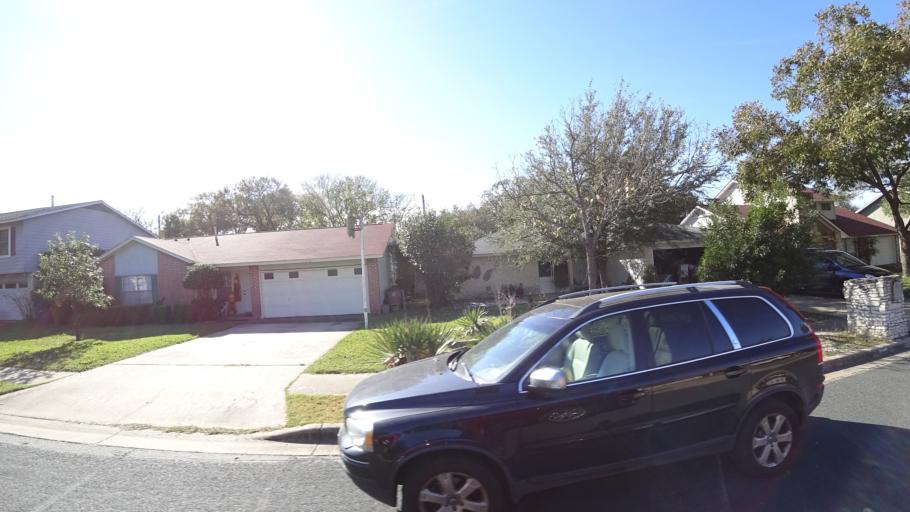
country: US
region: Texas
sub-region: Williamson County
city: Jollyville
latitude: 30.4250
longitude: -97.7765
